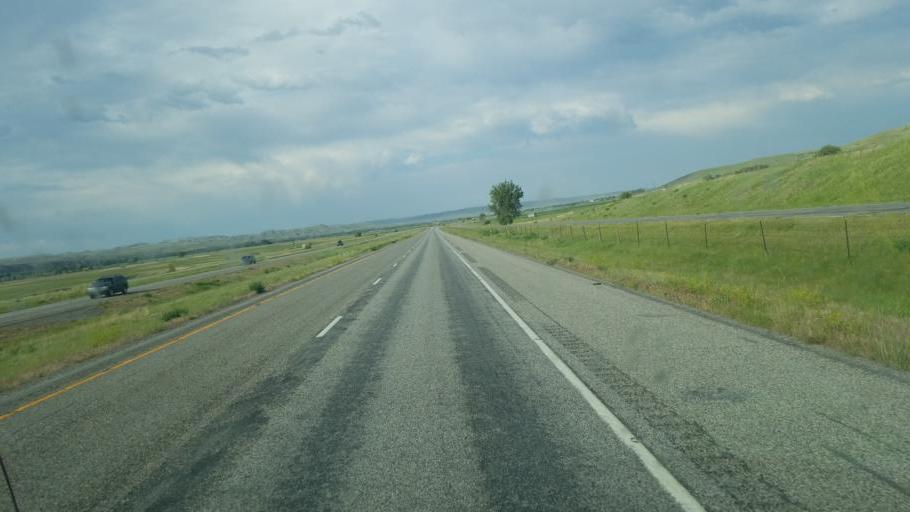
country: US
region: Montana
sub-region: Sweet Grass County
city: Big Timber
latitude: 45.7988
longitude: -110.0272
